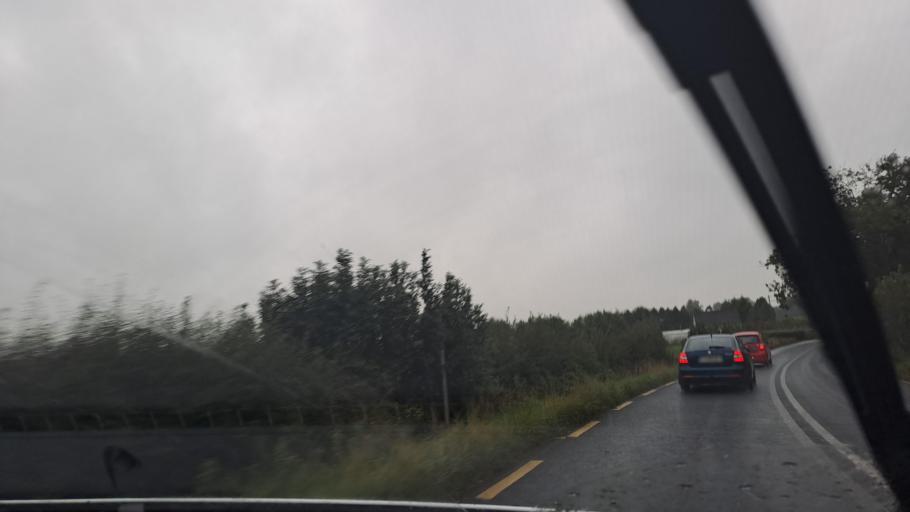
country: IE
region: Leinster
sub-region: Lu
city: Dundalk
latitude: 53.9892
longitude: -6.4754
